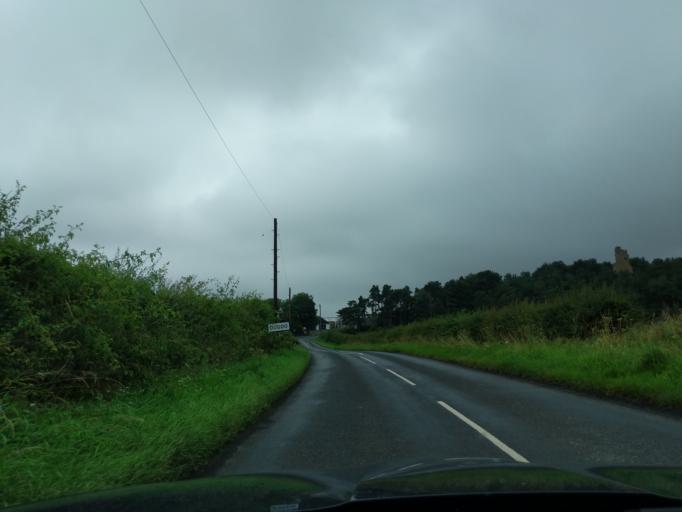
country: GB
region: England
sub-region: Northumberland
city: Ford
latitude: 55.6750
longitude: -2.1015
